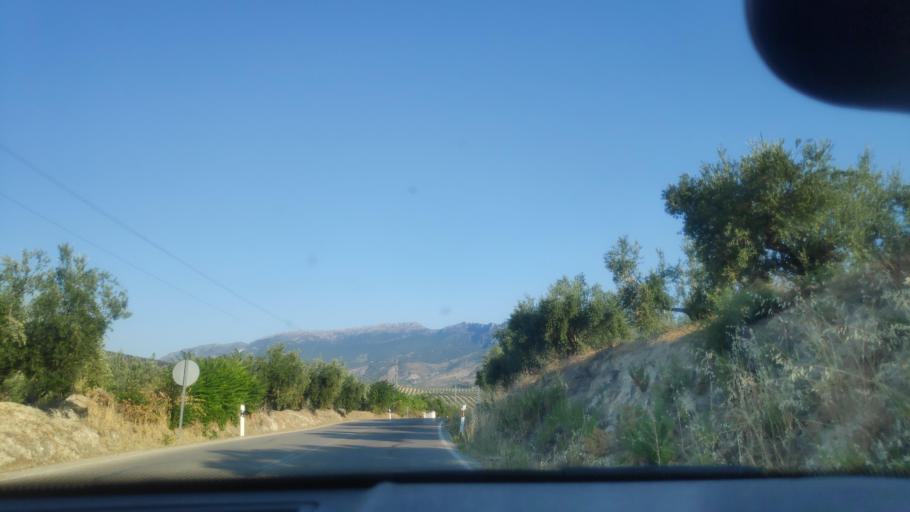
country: ES
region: Andalusia
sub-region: Provincia de Jaen
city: Jaen
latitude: 37.7299
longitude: -3.7637
